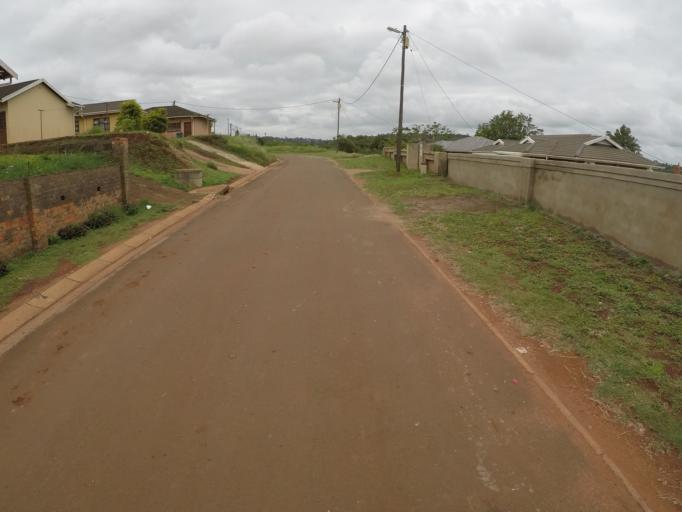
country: ZA
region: KwaZulu-Natal
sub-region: uThungulu District Municipality
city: Empangeni
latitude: -28.7734
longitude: 31.8835
